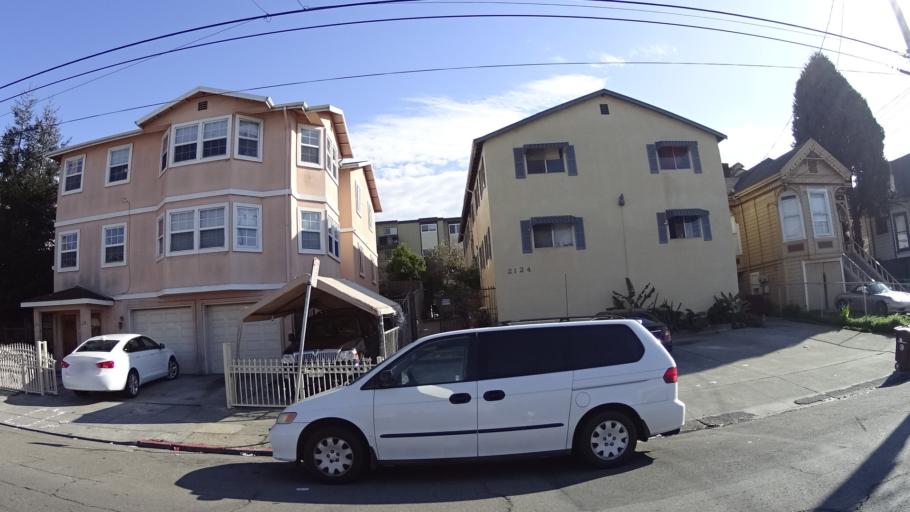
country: US
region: California
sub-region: Alameda County
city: Alameda
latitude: 37.7892
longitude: -122.2313
